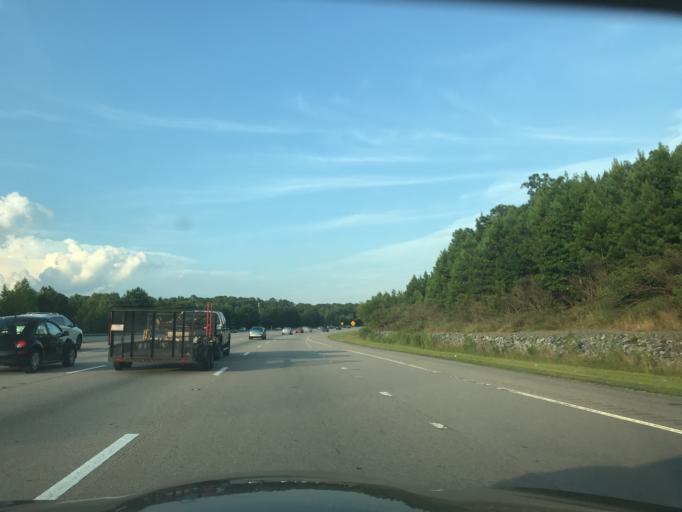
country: US
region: North Carolina
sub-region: Wake County
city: Morrisville
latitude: 35.9098
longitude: -78.7592
